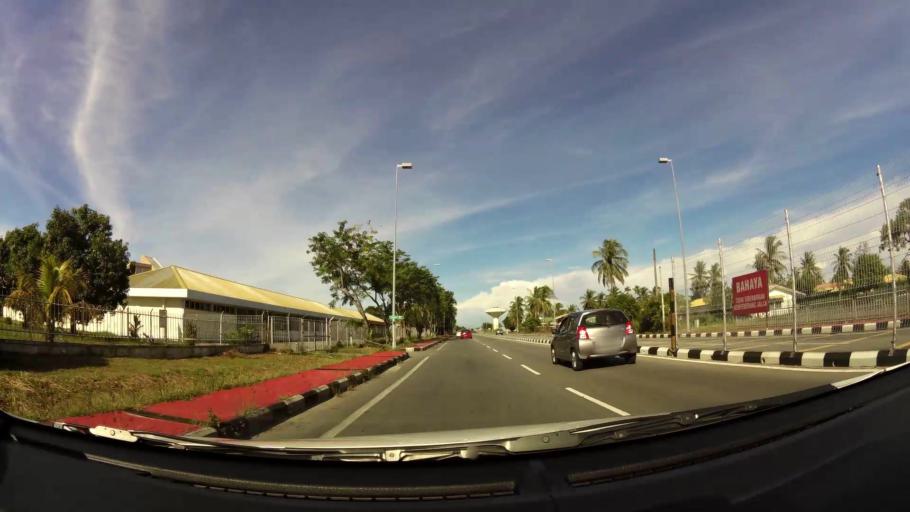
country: BN
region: Belait
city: Kuala Belait
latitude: 4.5779
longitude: 114.2051
